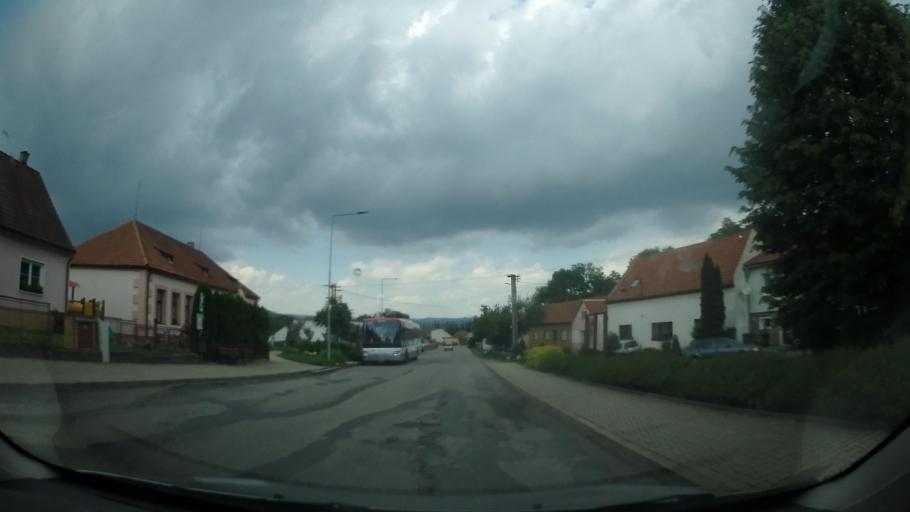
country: CZ
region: South Moravian
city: Svitavka
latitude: 49.4662
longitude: 16.6051
